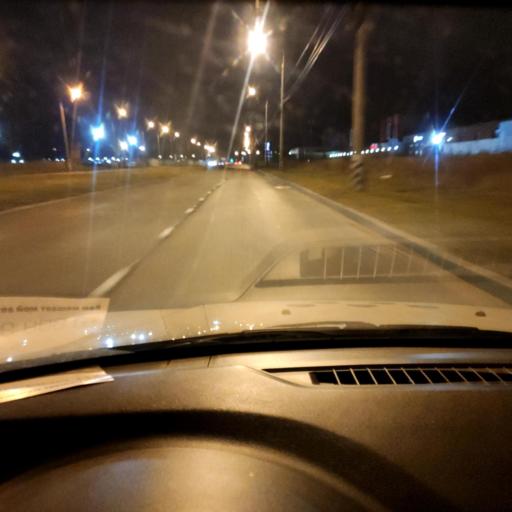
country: RU
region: Samara
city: Tol'yatti
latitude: 53.5569
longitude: 49.3370
